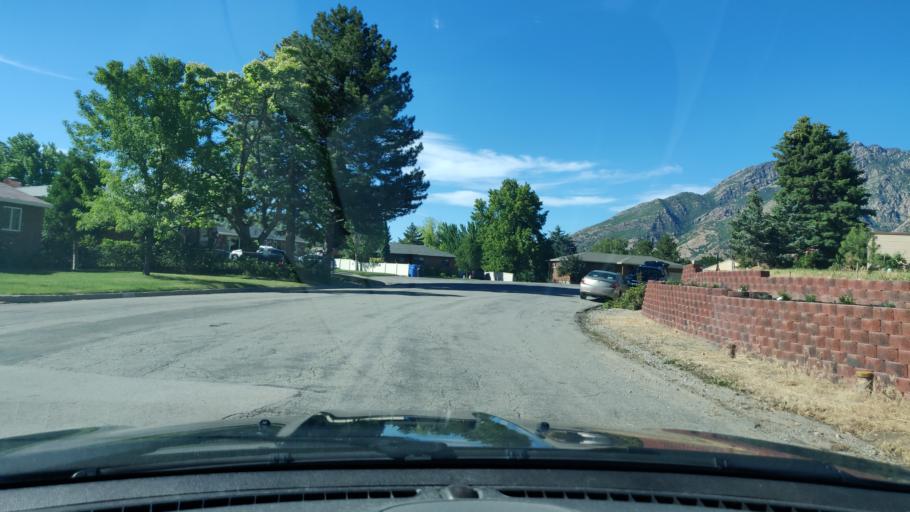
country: US
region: Utah
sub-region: Salt Lake County
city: Cottonwood Heights
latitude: 40.6109
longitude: -111.8147
